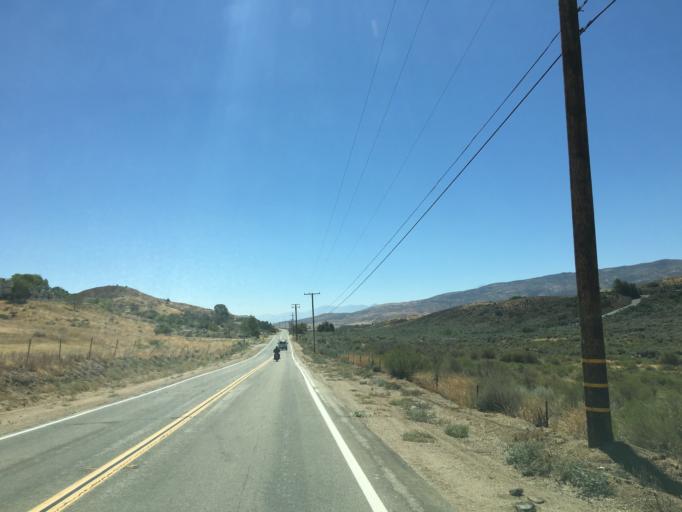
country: US
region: California
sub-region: Los Angeles County
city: Leona Valley
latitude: 34.6253
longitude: -118.3077
